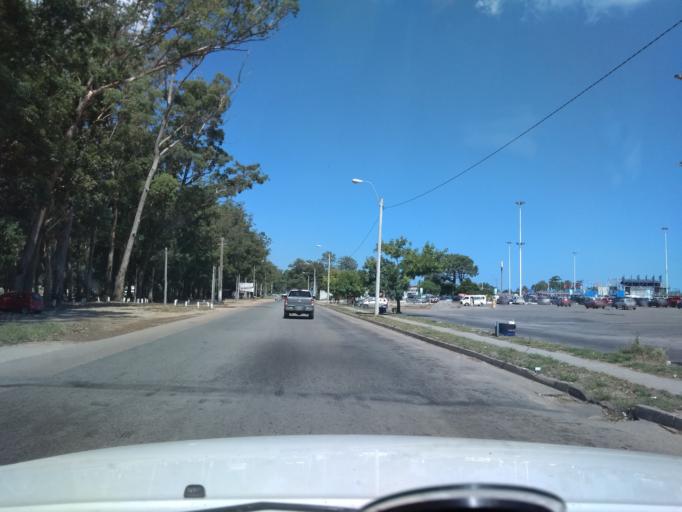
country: UY
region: Canelones
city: Barra de Carrasco
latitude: -34.8642
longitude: -56.0233
